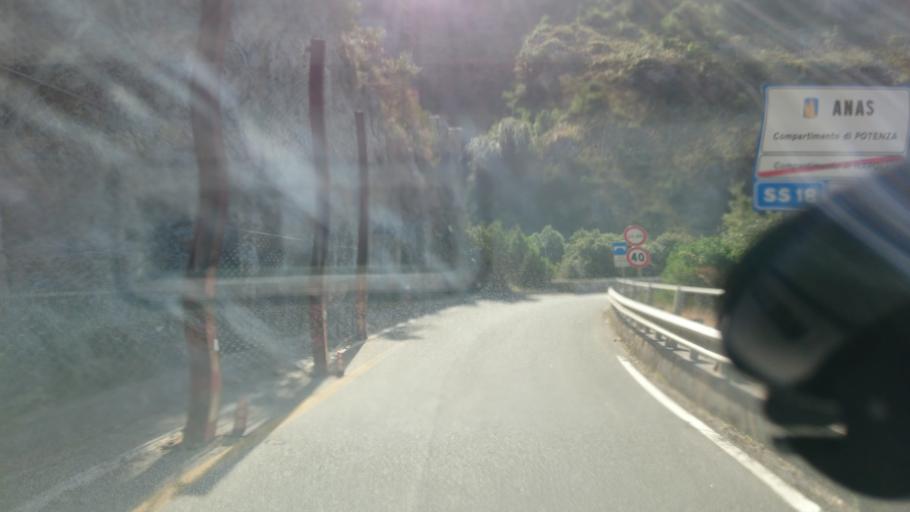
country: IT
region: Campania
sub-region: Provincia di Salerno
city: Sapri
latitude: 40.0443
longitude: 15.6461
